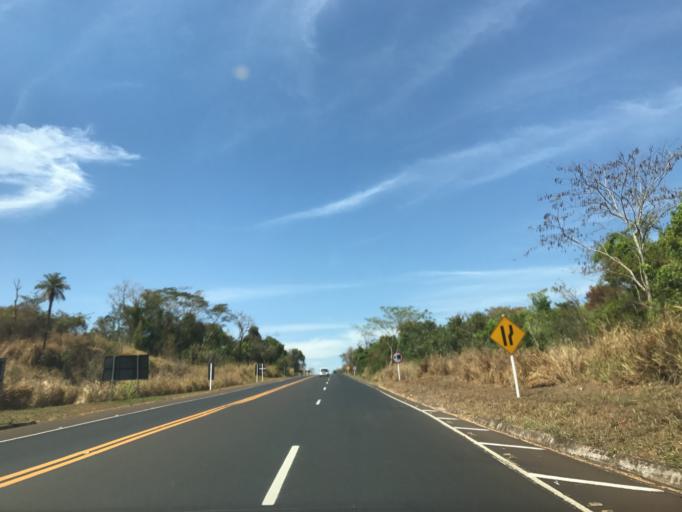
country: BR
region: Minas Gerais
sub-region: Monte Alegre De Minas
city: Monte Alegre de Minas
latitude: -19.0504
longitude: -49.0113
